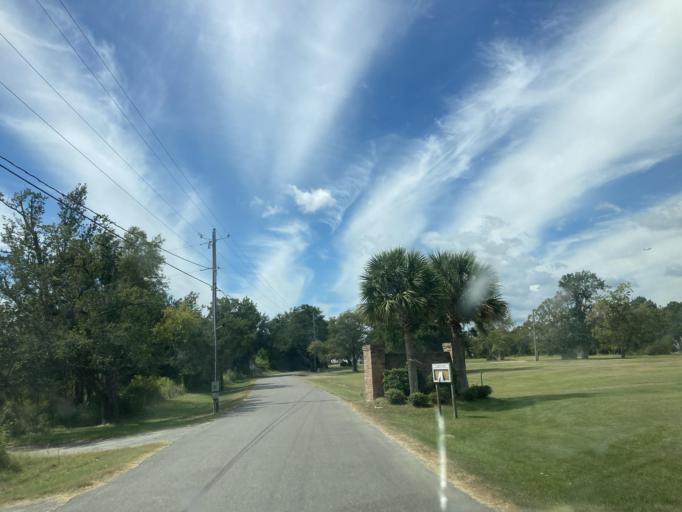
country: US
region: Mississippi
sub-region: Jackson County
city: Saint Martin
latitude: 30.4261
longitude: -88.8759
